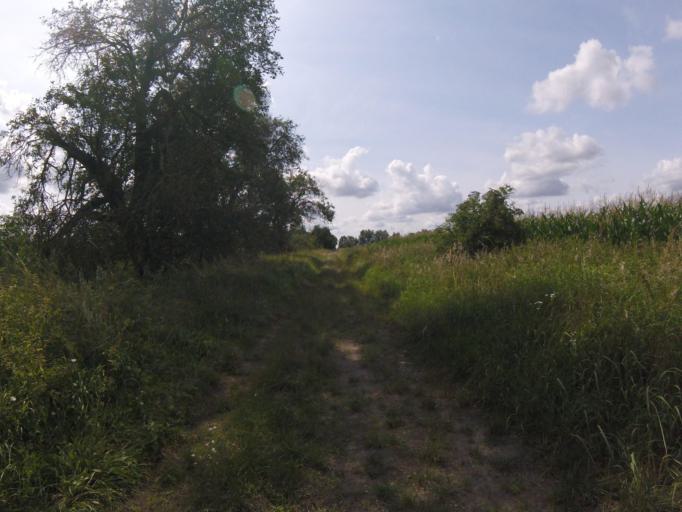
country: DE
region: Brandenburg
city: Mittenwalde
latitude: 52.2887
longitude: 13.5064
